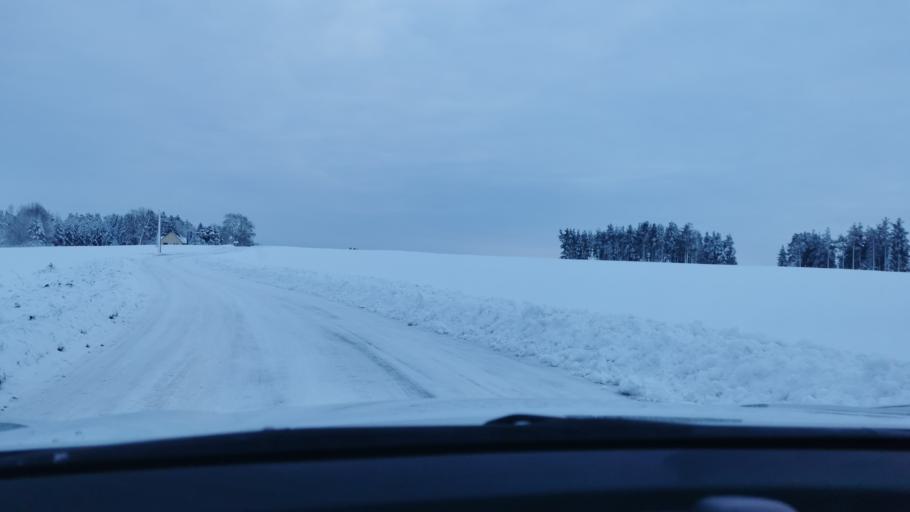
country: EE
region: Laeaene-Virumaa
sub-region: Viru-Nigula vald
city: Kunda
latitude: 59.4251
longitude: 26.5061
